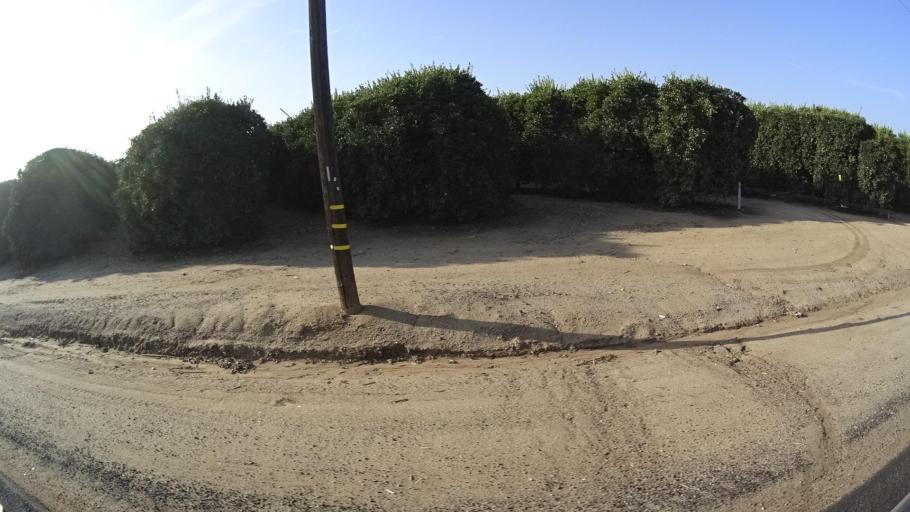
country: US
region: California
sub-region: Kern County
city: McFarland
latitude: 35.6724
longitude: -119.1324
